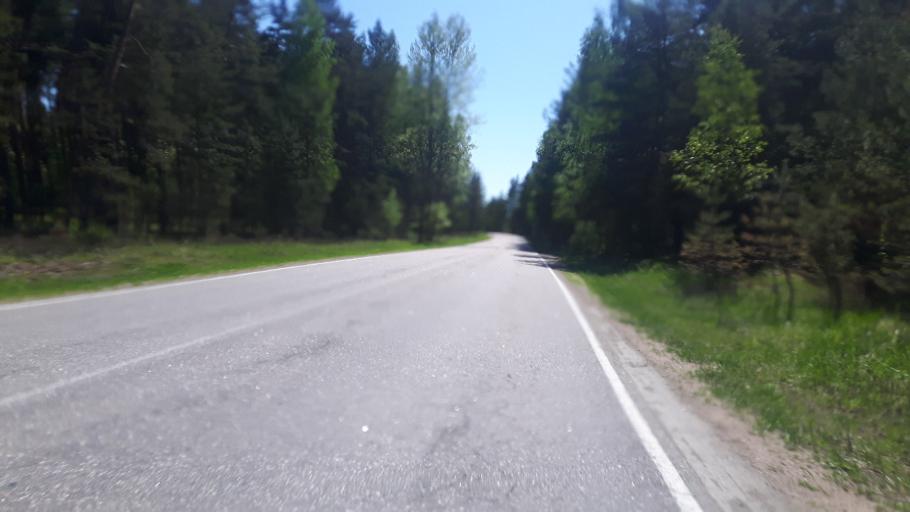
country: RU
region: Leningrad
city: Glebychevo
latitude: 60.3290
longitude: 28.8231
